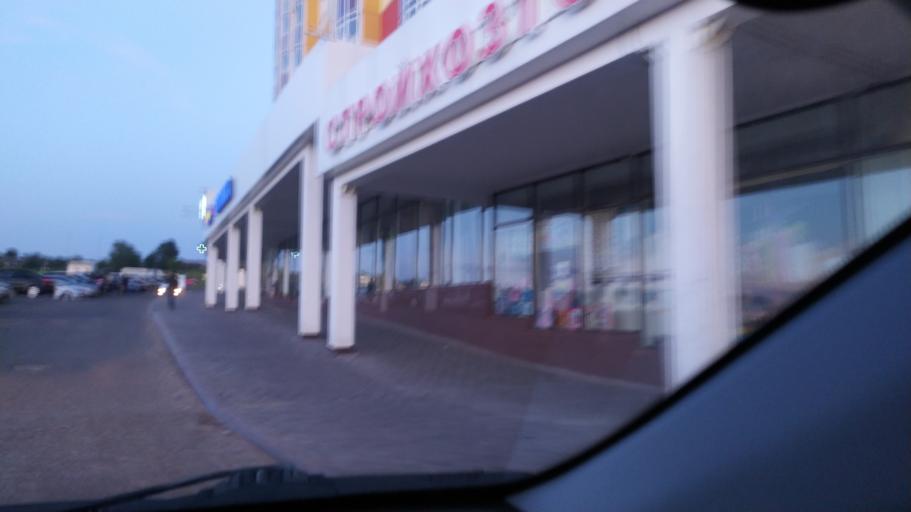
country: RU
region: Chuvashia
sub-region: Cheboksarskiy Rayon
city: Cheboksary
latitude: 56.1209
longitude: 47.2131
